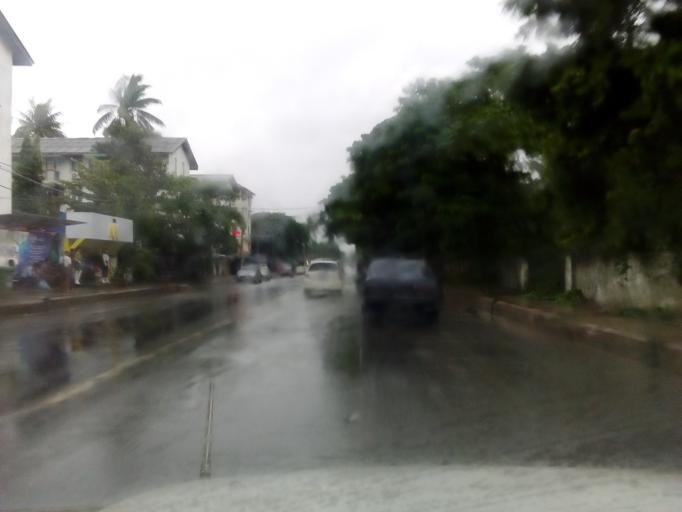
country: MM
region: Yangon
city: Yangon
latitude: 16.8249
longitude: 96.1646
